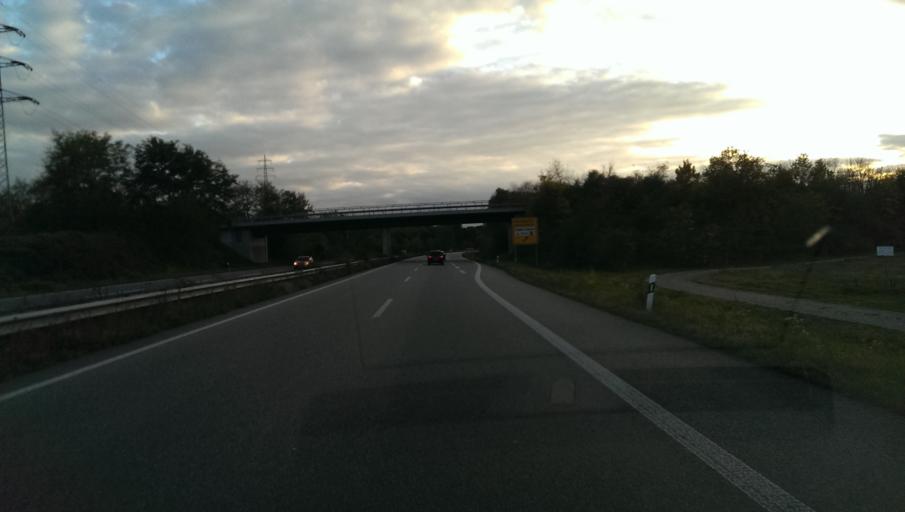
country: DE
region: Rheinland-Pfalz
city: Germersheim
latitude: 49.2088
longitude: 8.3492
